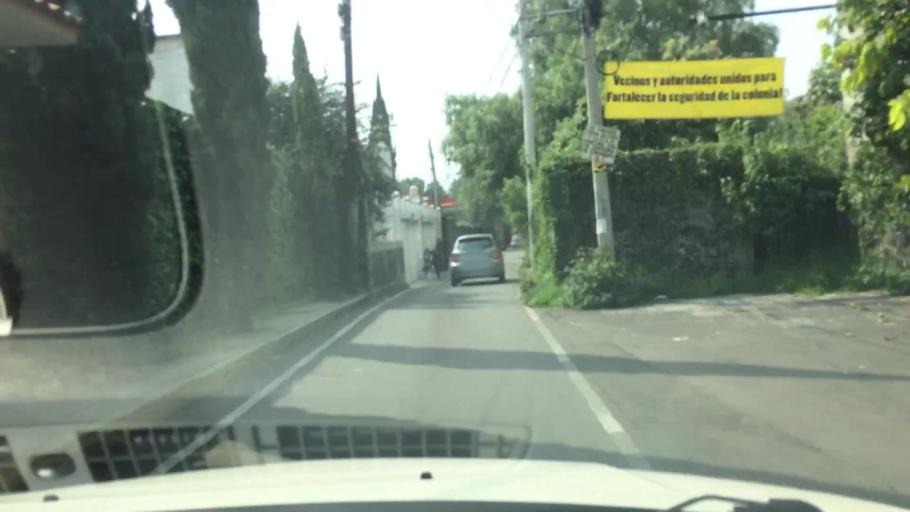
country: MX
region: Mexico City
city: Tlalpan
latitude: 19.2692
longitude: -99.1422
